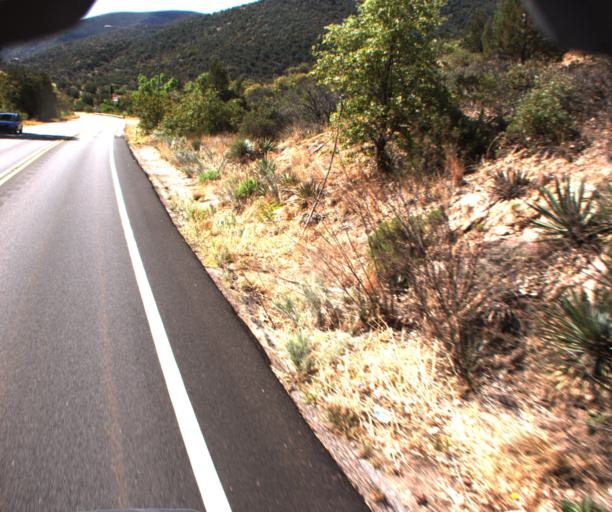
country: US
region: Arizona
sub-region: Cochise County
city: Bisbee
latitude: 31.4556
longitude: -109.9402
